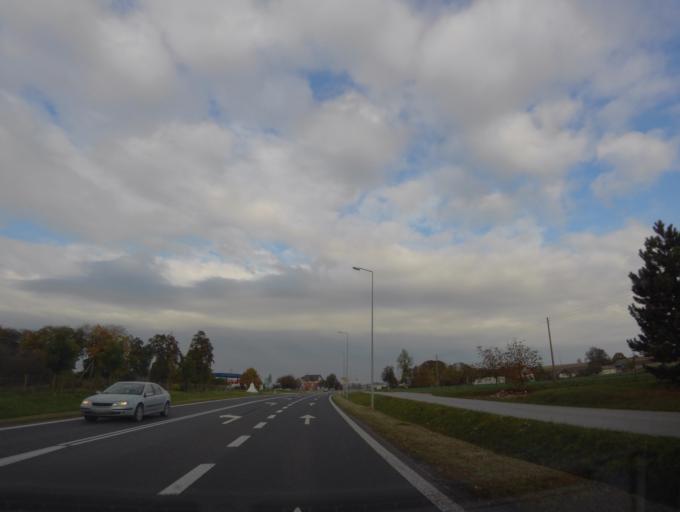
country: PL
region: Lublin Voivodeship
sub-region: Powiat lubelski
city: Wysokie
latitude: 50.8706
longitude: 22.6767
